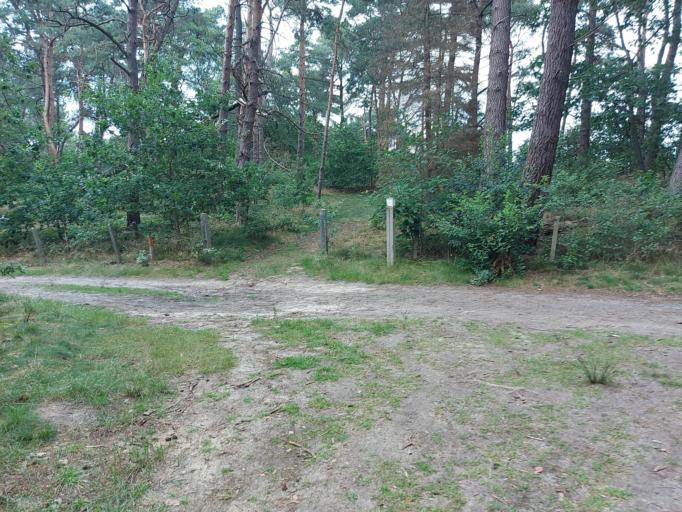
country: BE
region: Flanders
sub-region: Provincie Antwerpen
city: Meerhout
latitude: 51.1563
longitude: 5.0540
